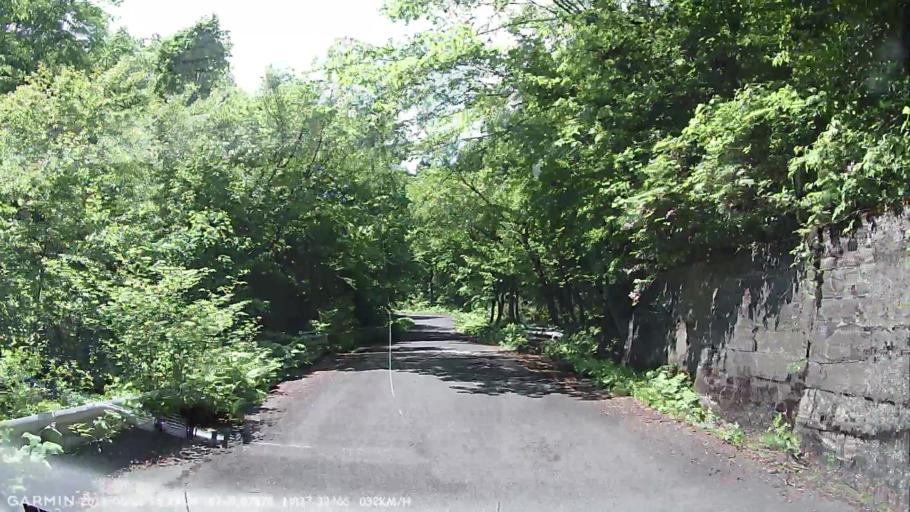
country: JP
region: Fukushima
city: Inawashiro
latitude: 37.3247
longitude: 140.0787
